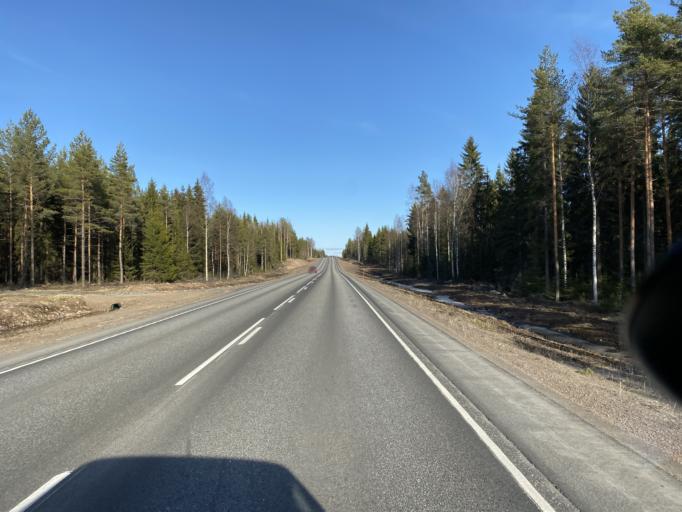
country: FI
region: Satakunta
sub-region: Rauma
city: Koeylioe
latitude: 61.1659
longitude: 22.3873
